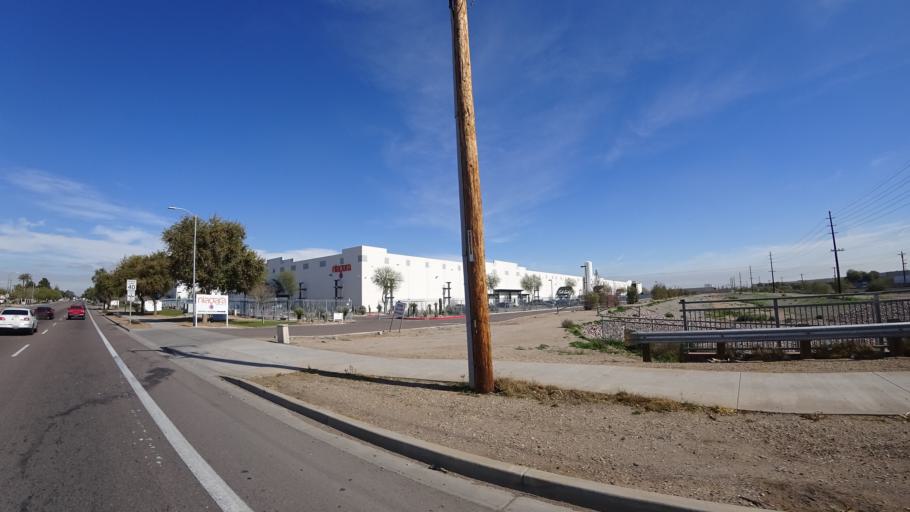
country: US
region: Arizona
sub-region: Maricopa County
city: Tolleson
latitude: 33.4448
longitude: -112.2035
